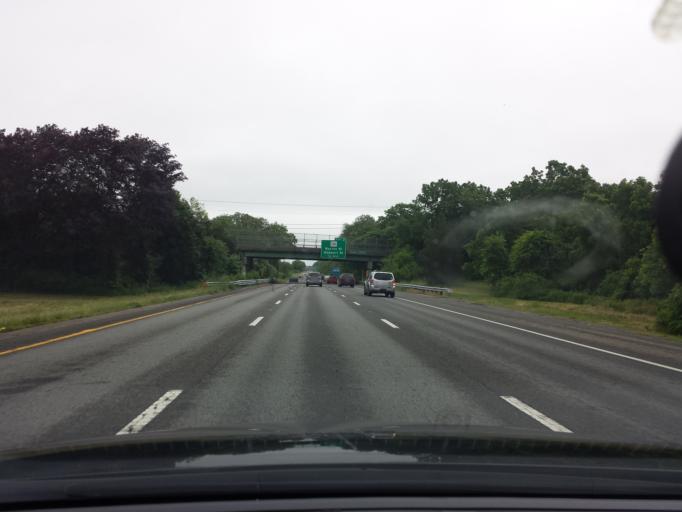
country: US
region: Rhode Island
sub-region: Bristol County
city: Warren
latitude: 41.7779
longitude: -71.2767
